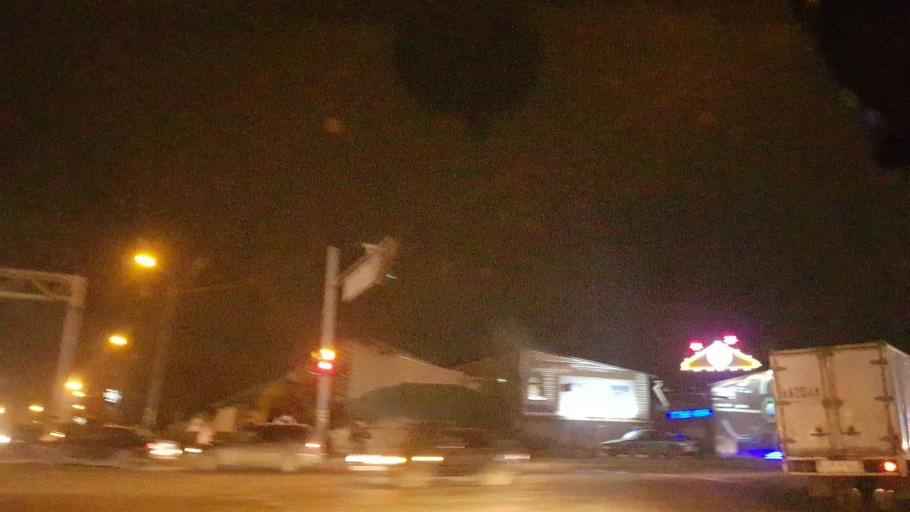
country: KZ
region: Almaty Oblysy
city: Pervomayskiy
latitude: 43.3512
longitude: 76.9252
